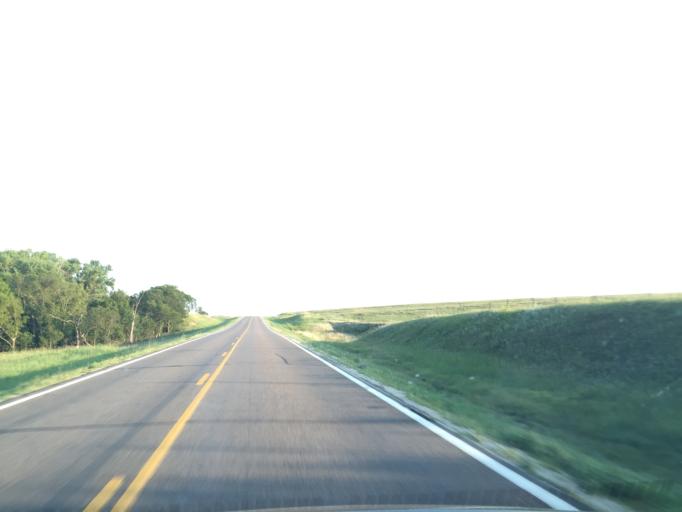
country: US
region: Kansas
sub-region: Ellsworth County
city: Ellsworth
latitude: 38.7883
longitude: -98.2250
